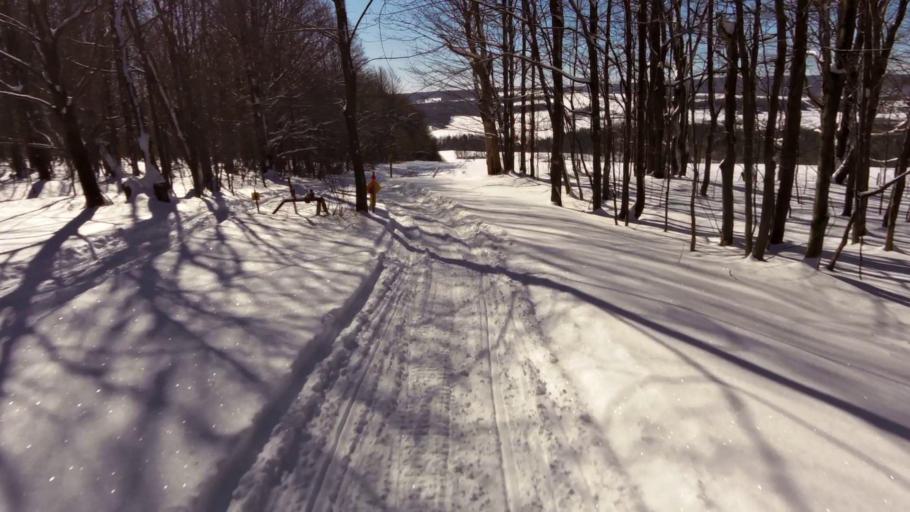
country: US
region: New York
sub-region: Chautauqua County
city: Silver Creek
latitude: 42.3810
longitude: -79.1497
